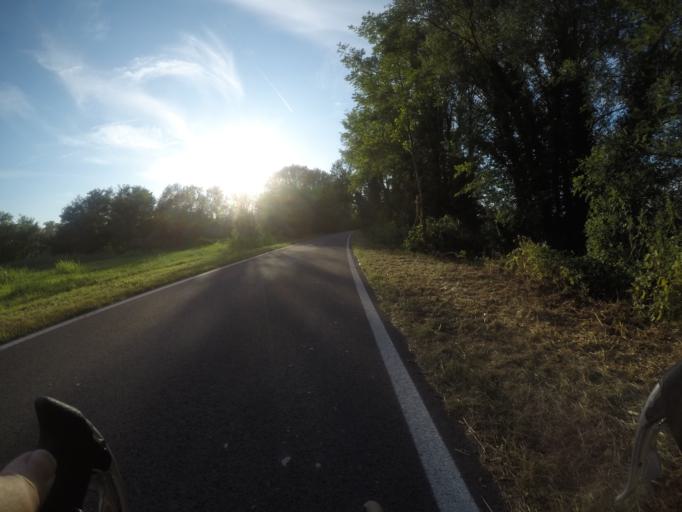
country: IT
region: Veneto
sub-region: Provincia di Rovigo
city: Pincara
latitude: 44.9957
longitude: 11.5911
